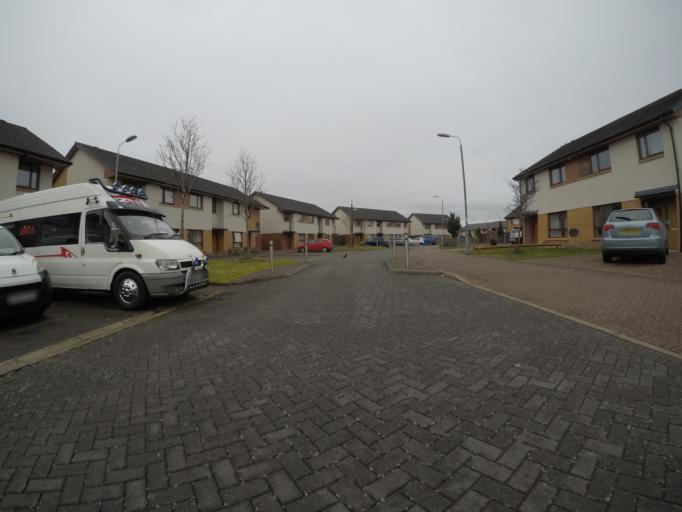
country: GB
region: Scotland
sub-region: North Ayrshire
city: Irvine
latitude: 55.6248
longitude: -4.6687
